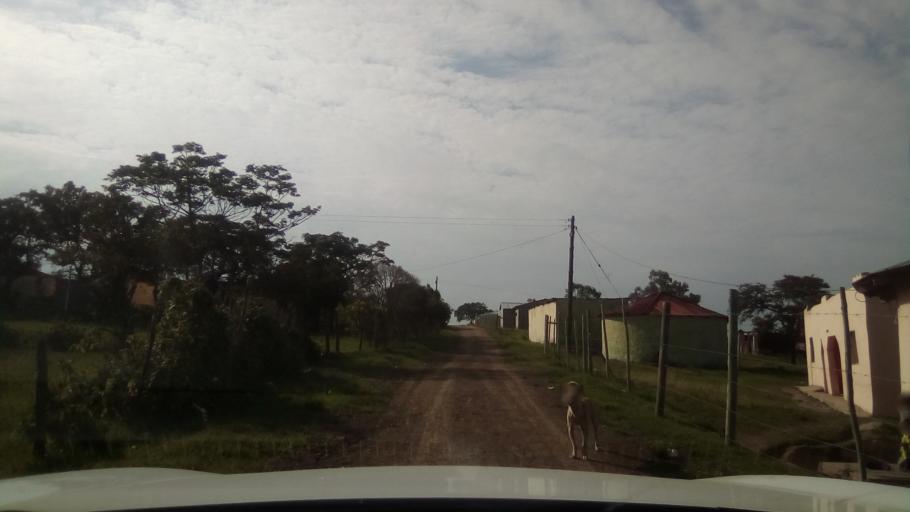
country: ZA
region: Eastern Cape
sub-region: Buffalo City Metropolitan Municipality
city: Bhisho
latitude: -33.0075
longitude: 27.3009
